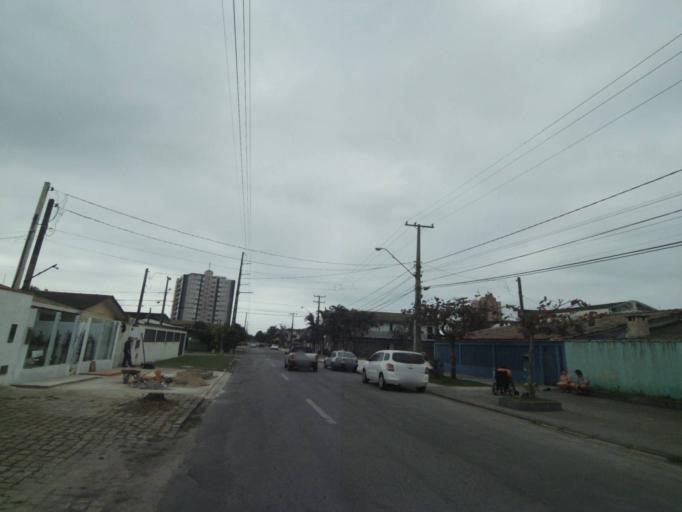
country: BR
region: Parana
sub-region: Paranagua
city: Paranagua
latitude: -25.5206
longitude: -48.5208
